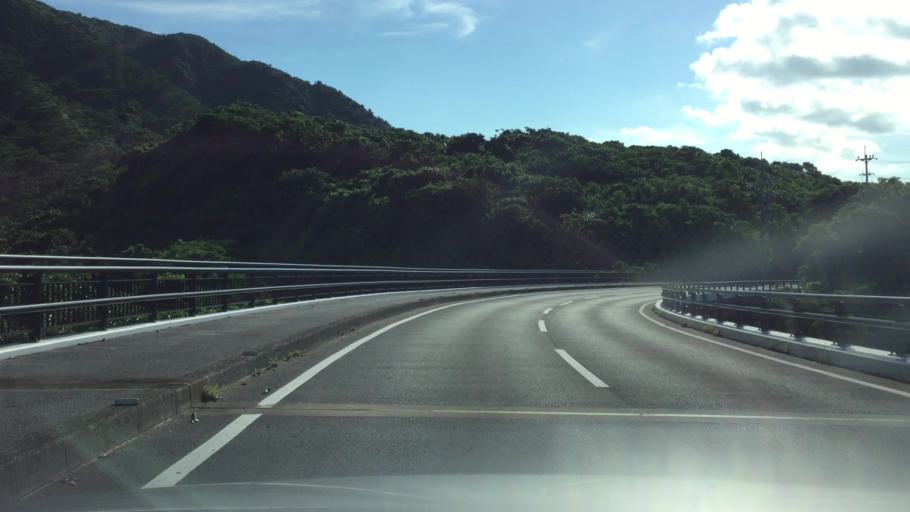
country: JP
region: Okinawa
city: Ishigaki
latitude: 24.4454
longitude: 124.1740
